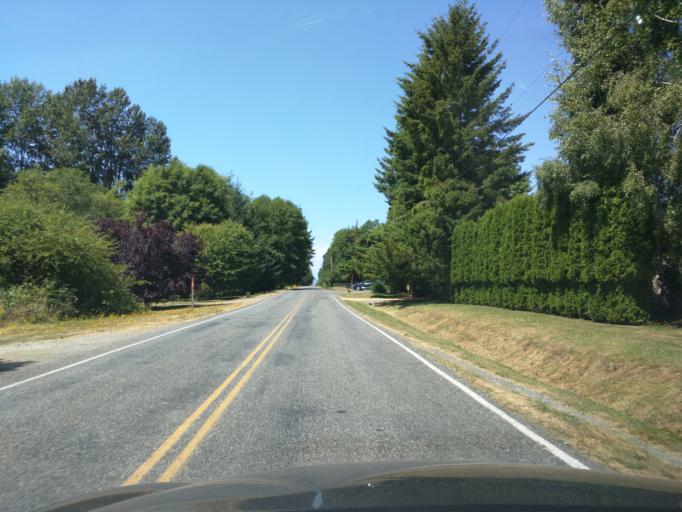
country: US
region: Washington
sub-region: Whatcom County
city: Blaine
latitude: 48.9940
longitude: -122.7040
